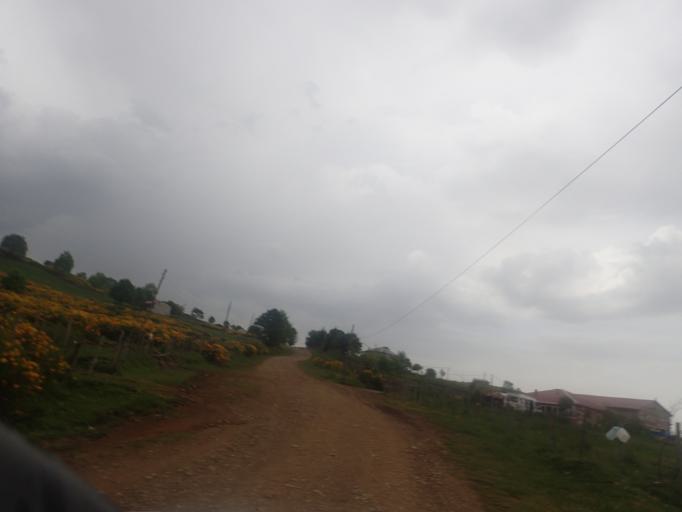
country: TR
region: Ordu
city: Topcam
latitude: 40.6675
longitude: 37.9328
